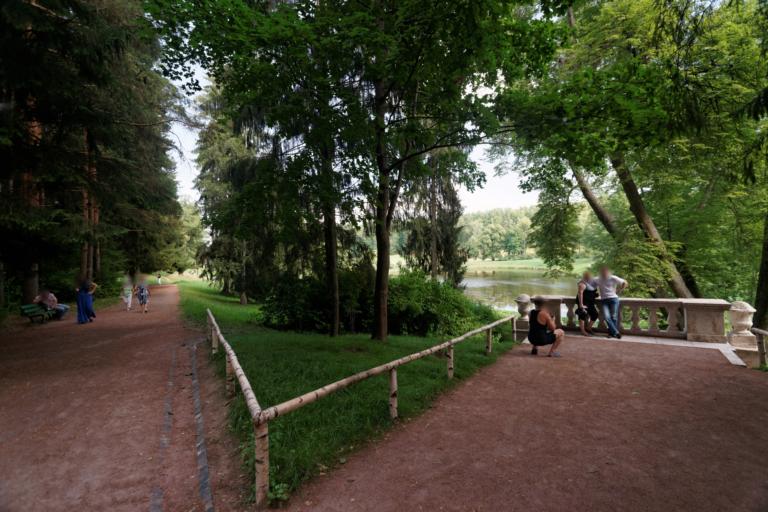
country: RU
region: St.-Petersburg
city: Tyarlevo
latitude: 59.6897
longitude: 30.4547
